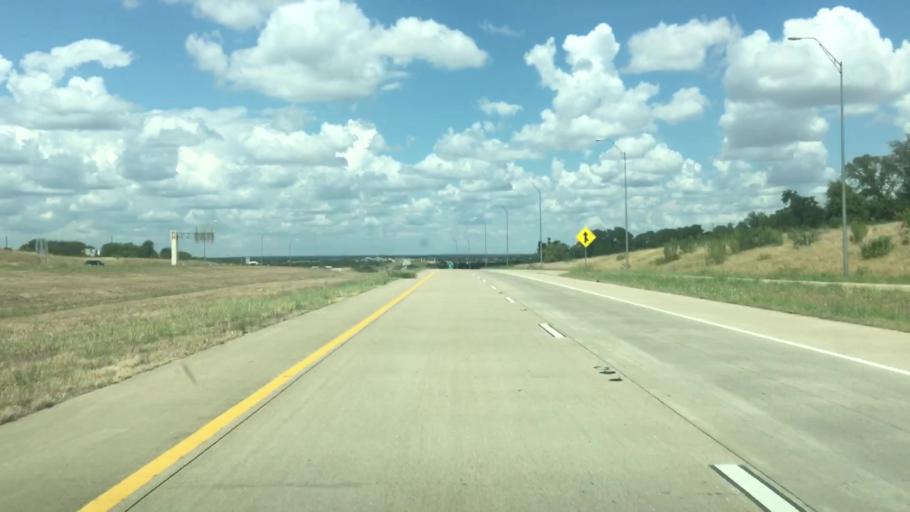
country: US
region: Texas
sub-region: Williamson County
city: Georgetown
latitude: 30.6463
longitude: -97.6318
